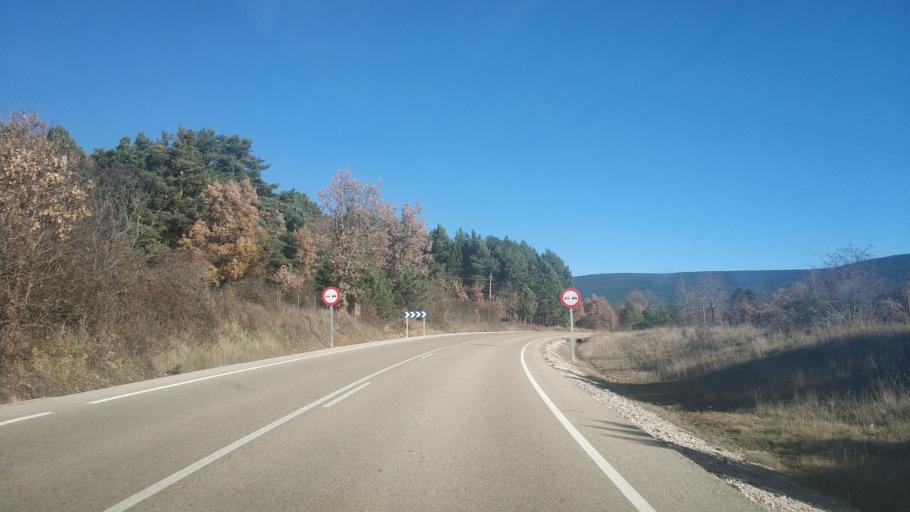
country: ES
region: Castille and Leon
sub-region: Provincia de Soria
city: Vinuesa
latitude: 41.8994
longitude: -2.7700
